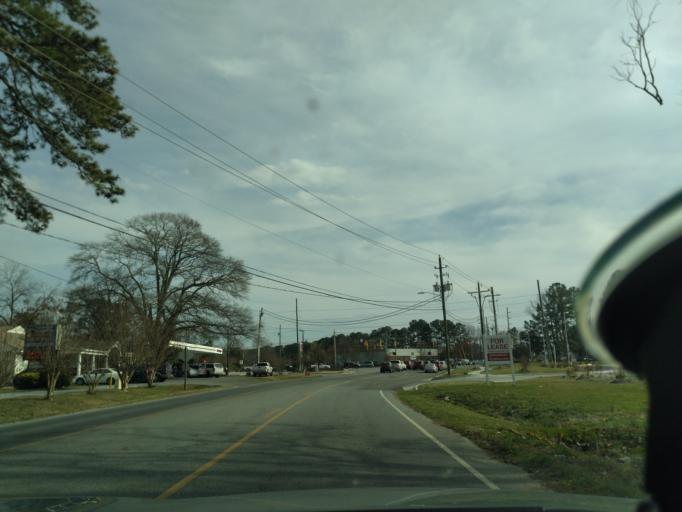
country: US
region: North Carolina
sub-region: Pitt County
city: Greenville
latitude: 35.5916
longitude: -77.3470
